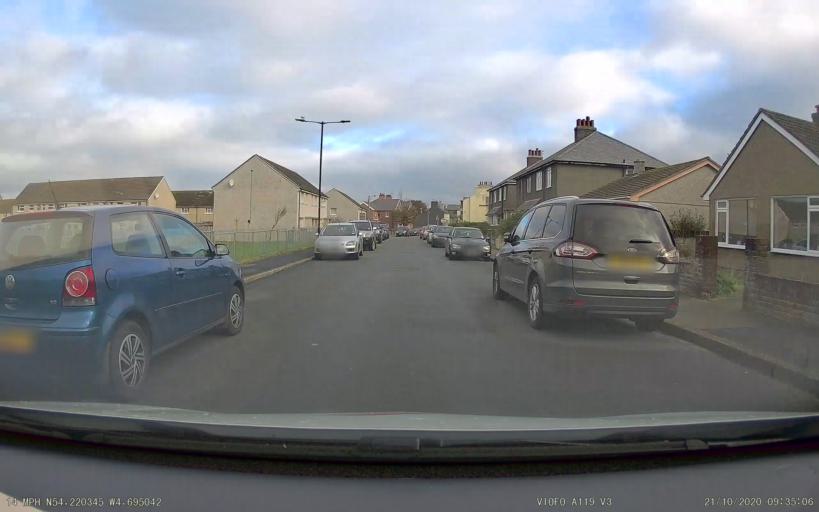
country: IM
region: Port Erin
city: Port Erin
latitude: 54.2204
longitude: -4.6950
